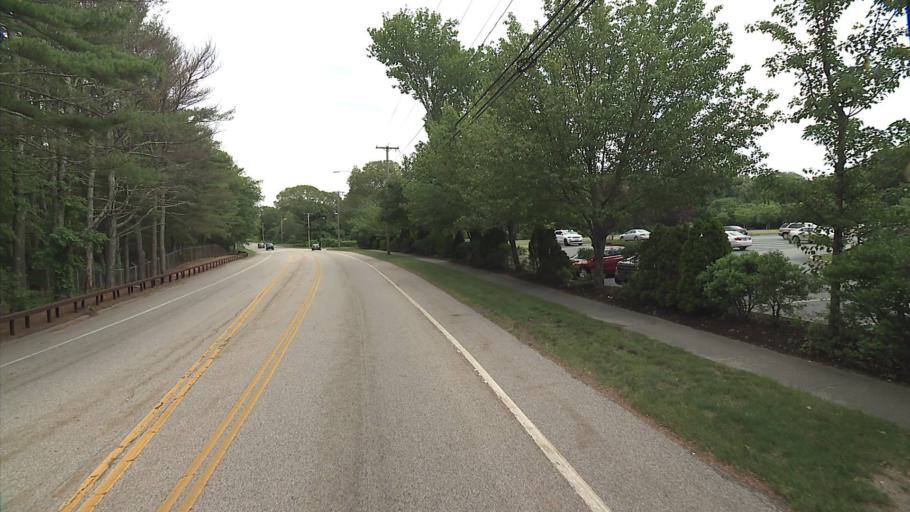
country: US
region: Connecticut
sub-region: New London County
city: Poquonock Bridge
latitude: 41.3657
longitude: -72.0262
